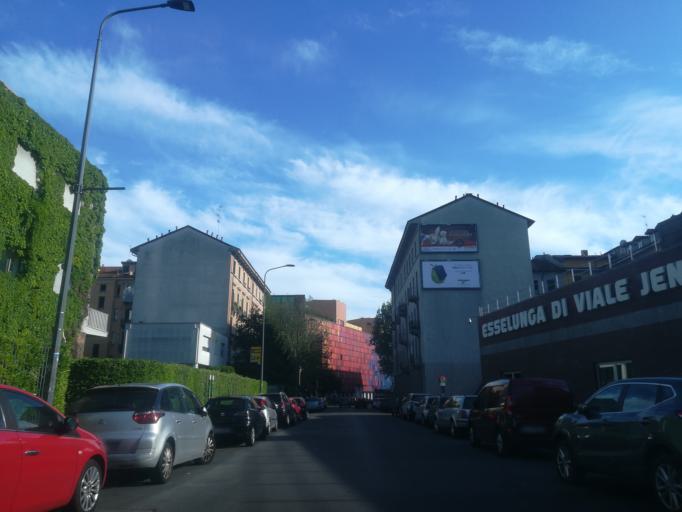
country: IT
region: Lombardy
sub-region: Citta metropolitana di Milano
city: Milano
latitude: 45.4982
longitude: 9.1817
